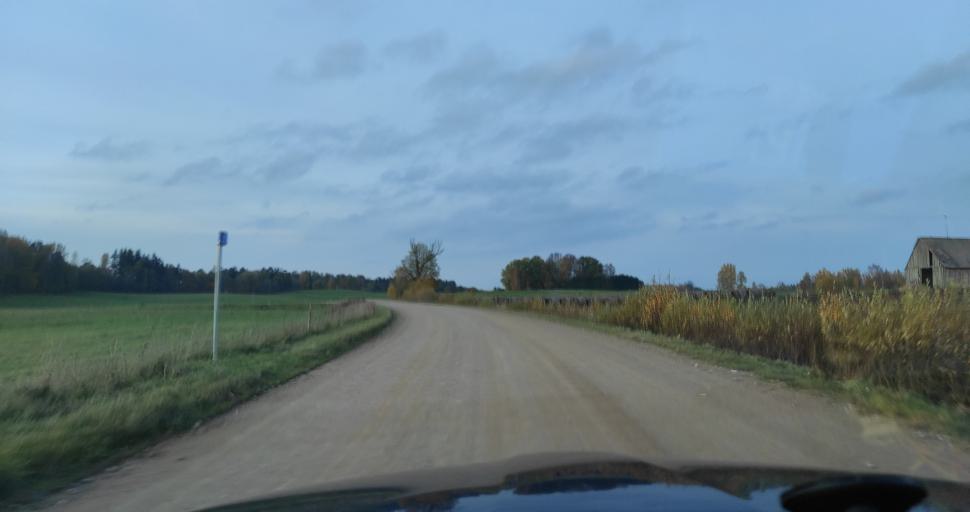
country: LV
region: Aizpute
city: Aizpute
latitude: 56.6510
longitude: 21.7958
